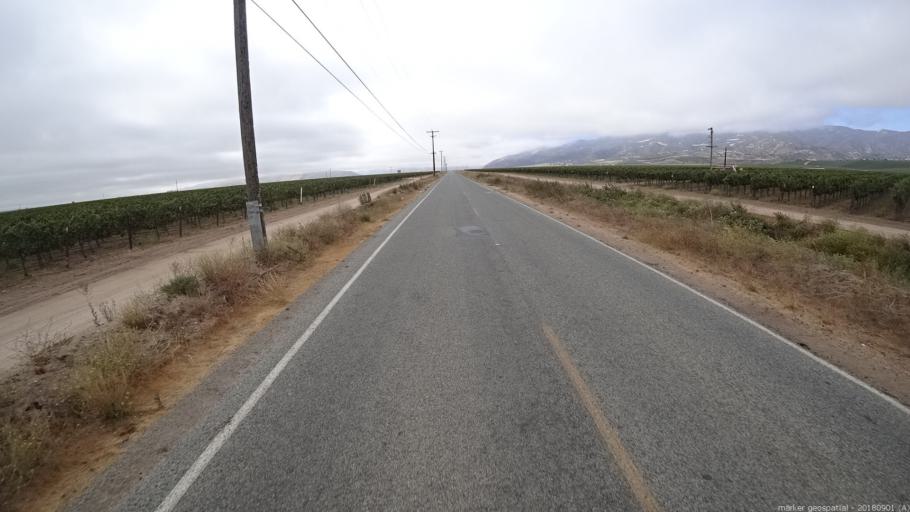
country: US
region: California
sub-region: Monterey County
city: Soledad
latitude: 36.3542
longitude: -121.3204
